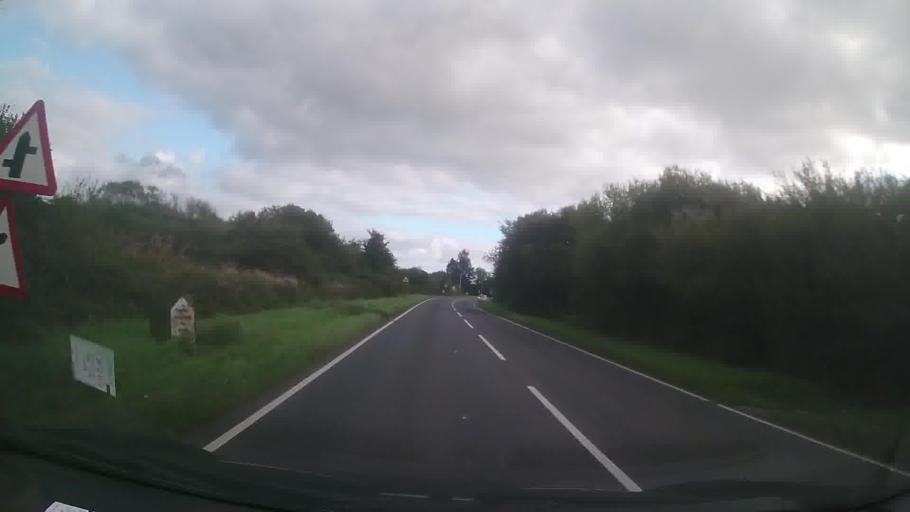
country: GB
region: Wales
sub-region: Pembrokeshire
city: Kilgetty
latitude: 51.7268
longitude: -4.7194
